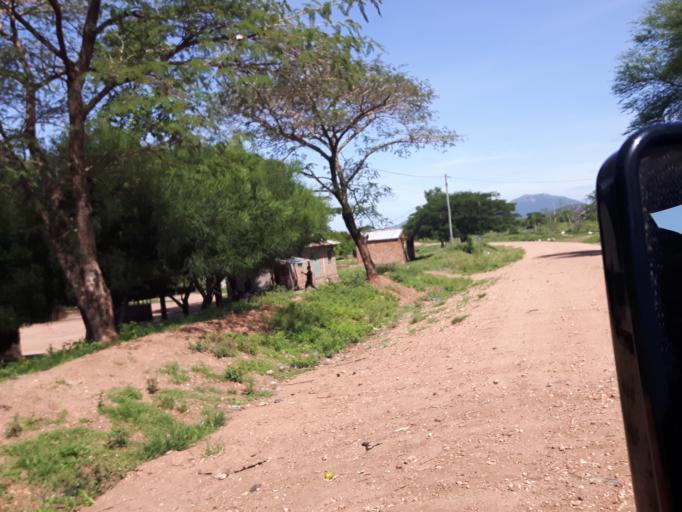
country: TZ
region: Mara
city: Issenye
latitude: -1.9608
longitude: 34.2698
